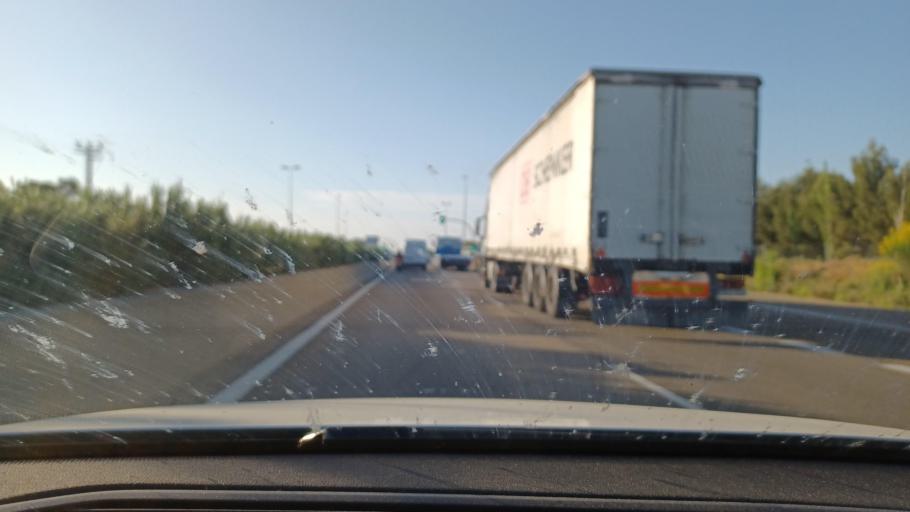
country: ES
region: Castille and Leon
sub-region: Provincia de Valladolid
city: Cisterniga
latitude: 41.6081
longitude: -4.7081
